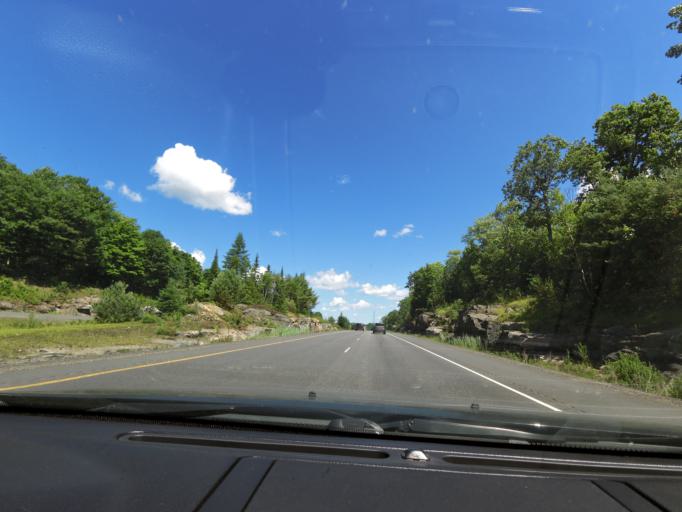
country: CA
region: Ontario
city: Bracebridge
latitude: 45.1868
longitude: -79.3124
